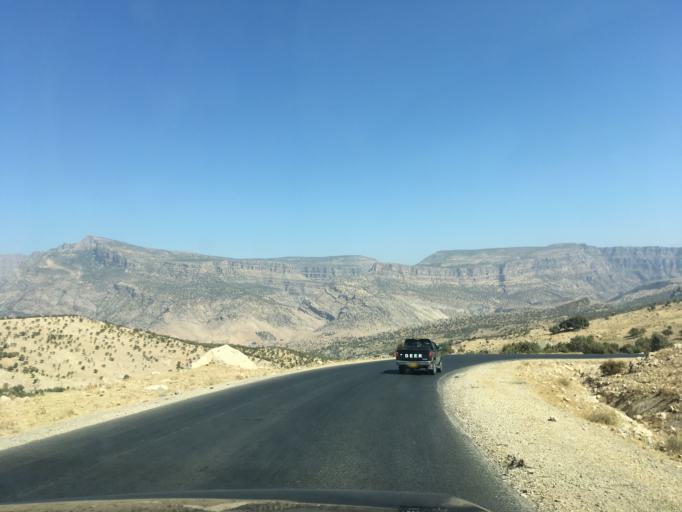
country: IQ
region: Arbil
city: Ruwandiz
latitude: 36.6432
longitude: 44.3409
